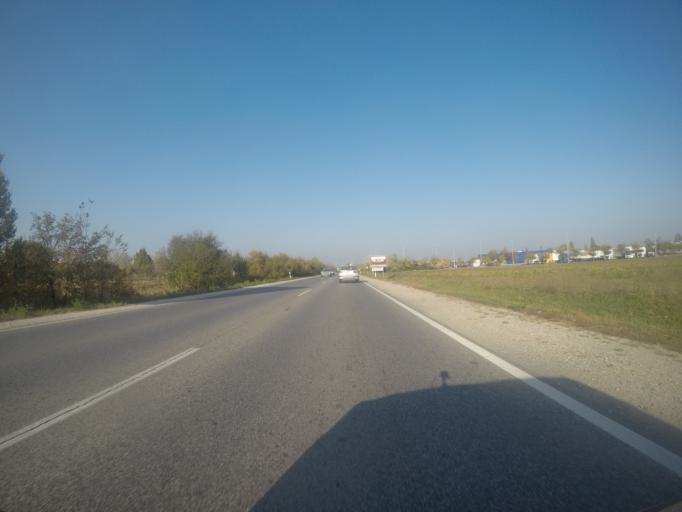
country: HU
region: Pest
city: Erd
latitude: 47.3749
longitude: 18.9340
